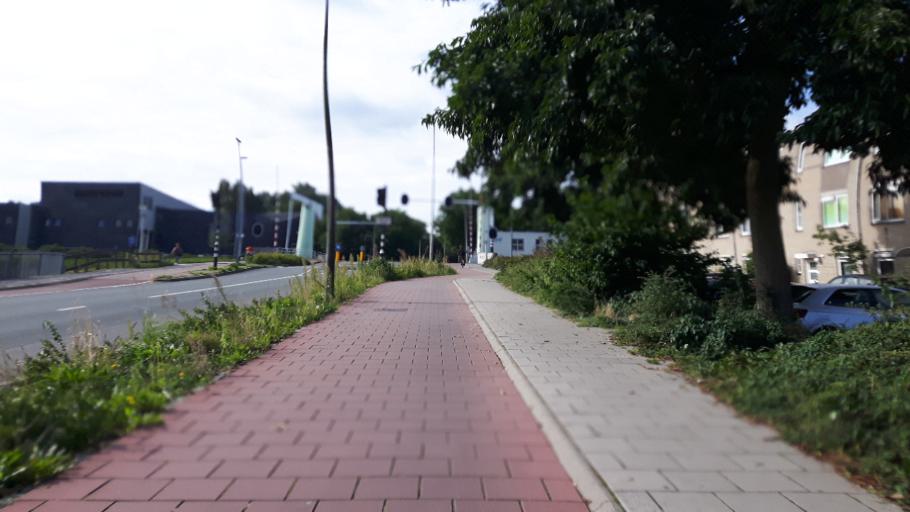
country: NL
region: North Holland
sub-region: Gemeente Purmerend
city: Purmerend
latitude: 52.5084
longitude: 4.9565
